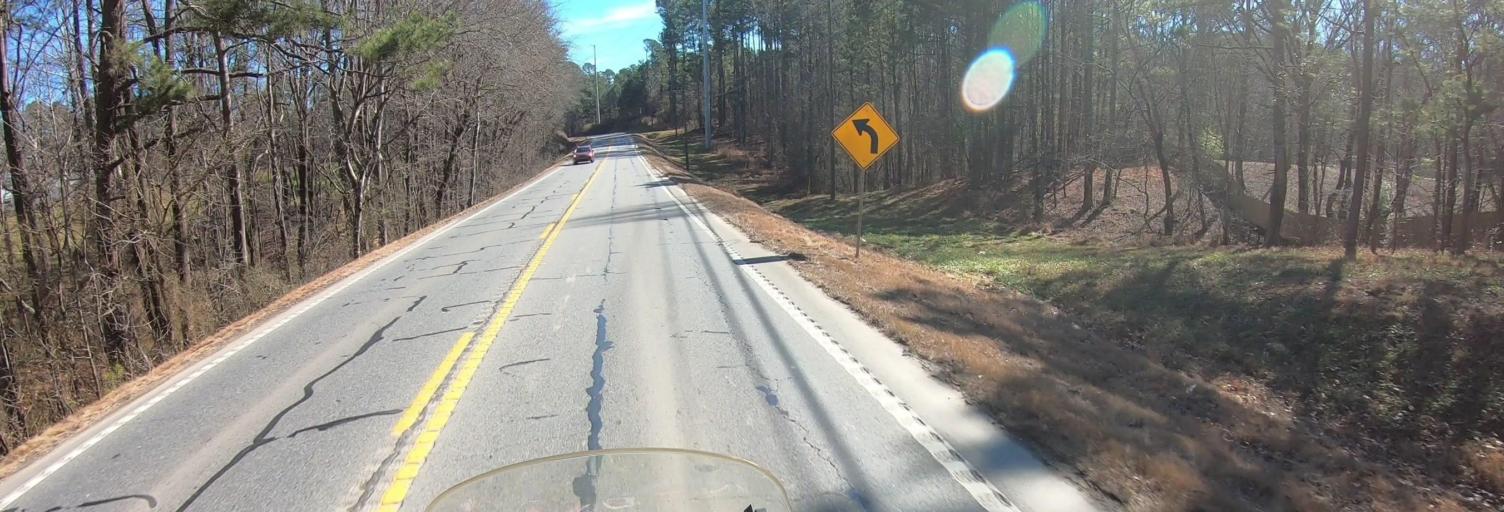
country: US
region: Georgia
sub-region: Forsyth County
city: Cumming
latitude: 34.3035
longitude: -84.1998
